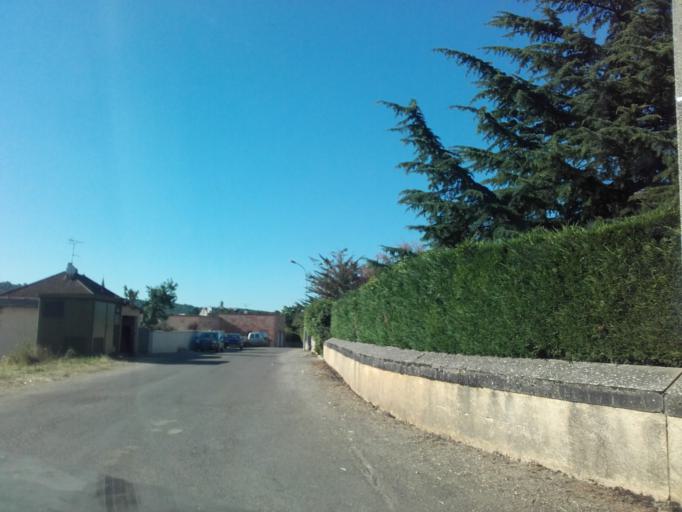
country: FR
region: Bourgogne
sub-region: Departement de Saone-et-Loire
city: Rully
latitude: 46.8688
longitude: 4.7420
